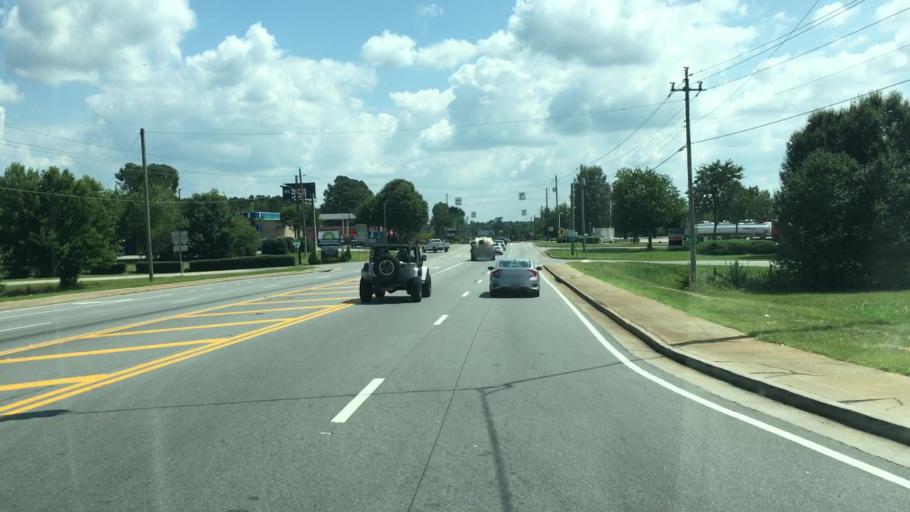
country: US
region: Georgia
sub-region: Morgan County
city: Madison
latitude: 33.5538
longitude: -83.4742
